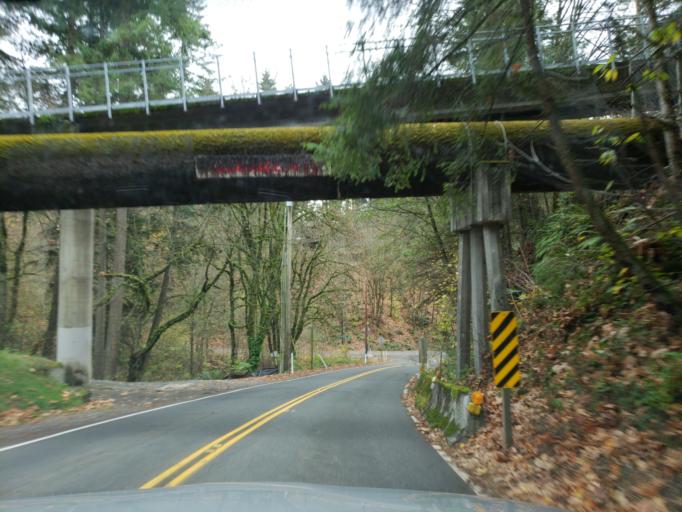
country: US
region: Washington
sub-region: King County
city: Woodinville
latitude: 47.7365
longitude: -122.1319
